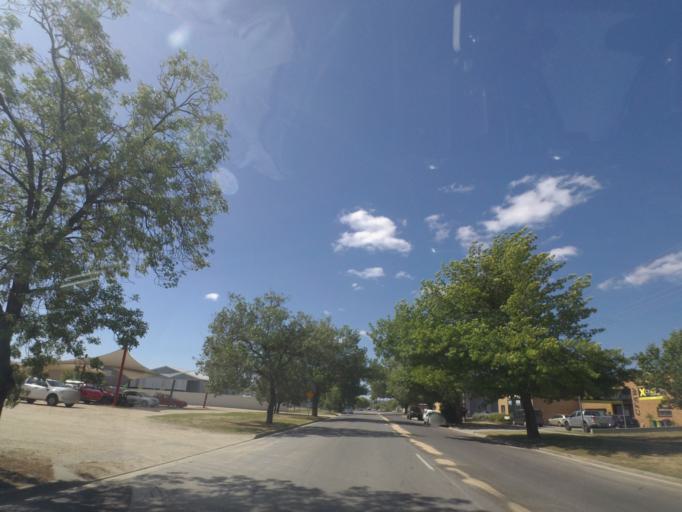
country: AU
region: New South Wales
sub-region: Albury Municipality
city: South Albury
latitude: -36.0922
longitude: 146.9135
